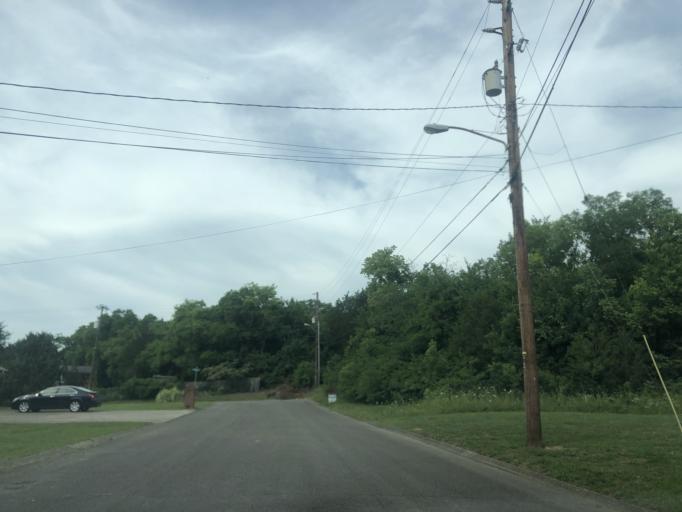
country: US
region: Tennessee
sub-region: Davidson County
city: Nashville
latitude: 36.2165
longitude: -86.8076
